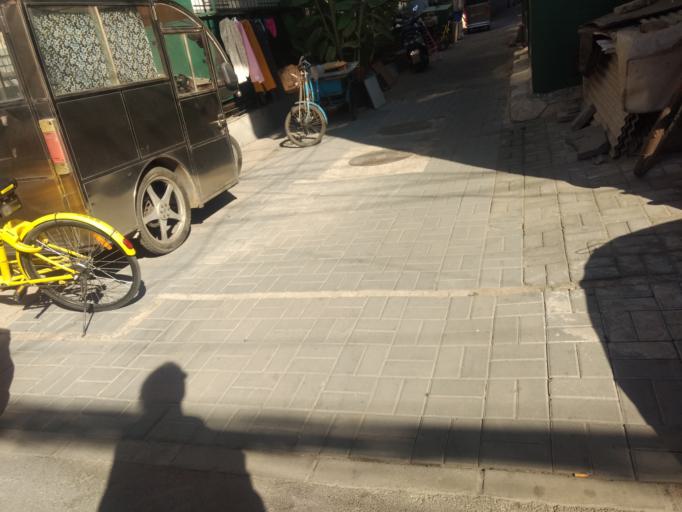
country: CN
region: Beijing
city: Beijing
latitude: 39.8935
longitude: 116.3817
